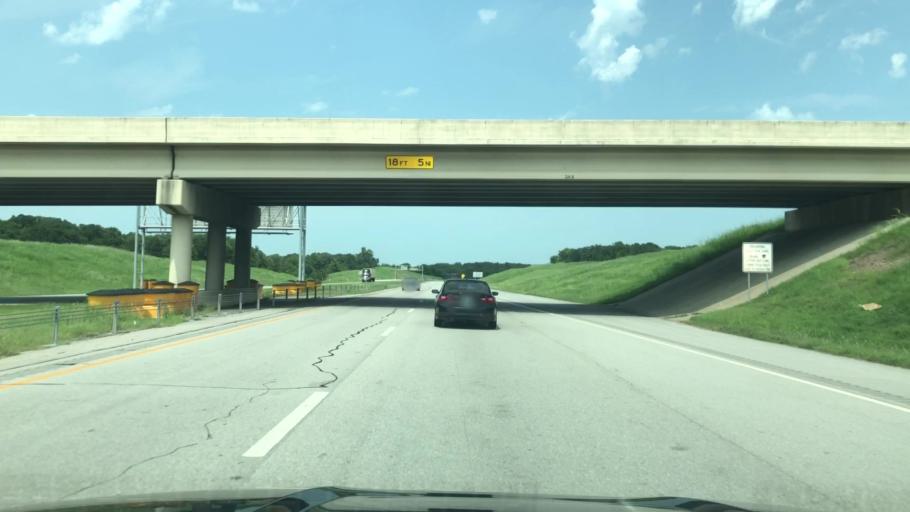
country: US
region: Oklahoma
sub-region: Rogers County
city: Catoosa
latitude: 36.1767
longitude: -95.7319
